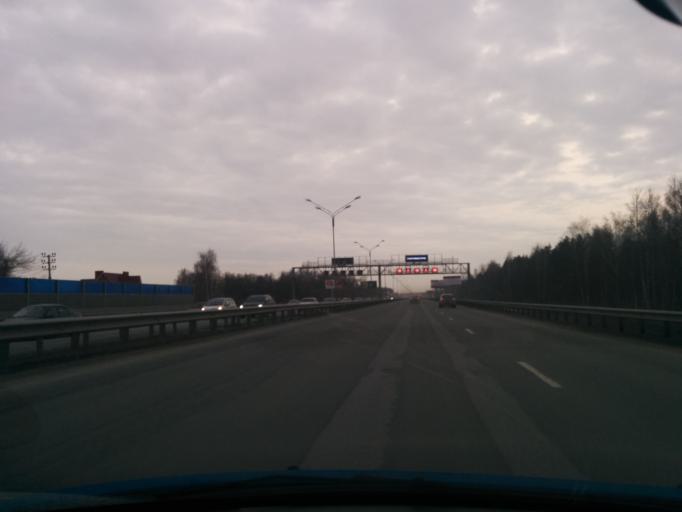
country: RU
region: Bashkortostan
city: Ufa
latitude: 54.6920
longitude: 55.9421
